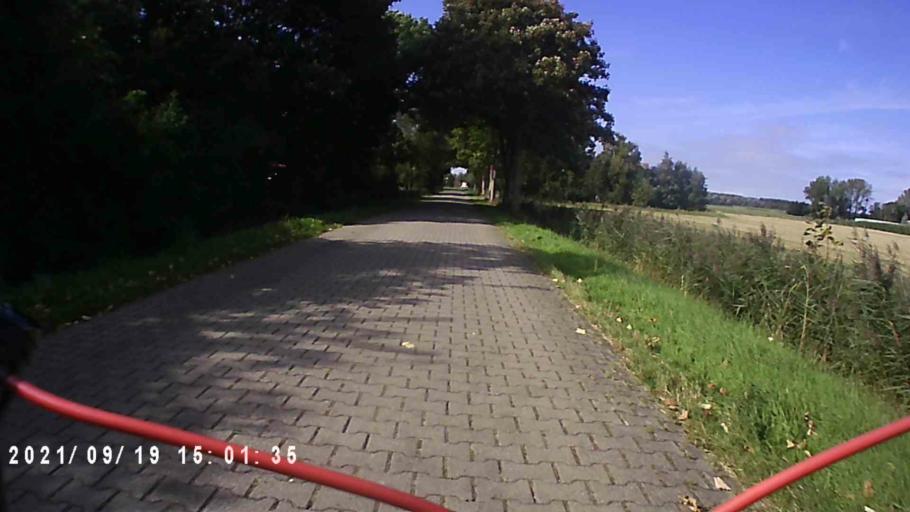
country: DE
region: Lower Saxony
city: Bunde
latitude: 53.1587
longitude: 7.2035
